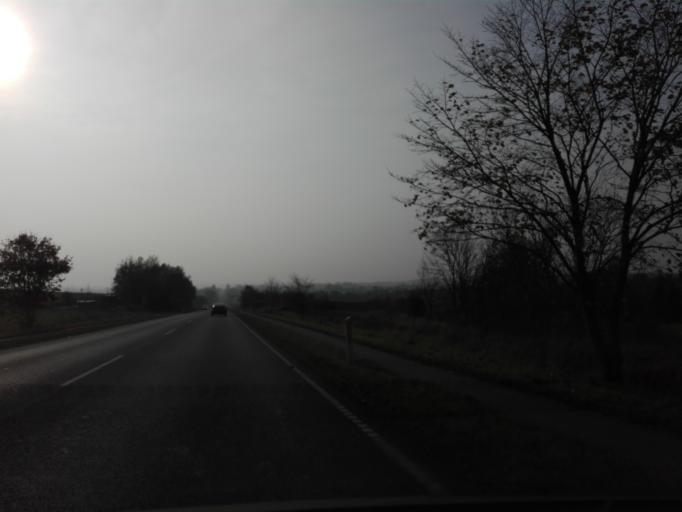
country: DK
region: Central Jutland
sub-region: Arhus Kommune
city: Malling
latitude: 56.0178
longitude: 10.1775
